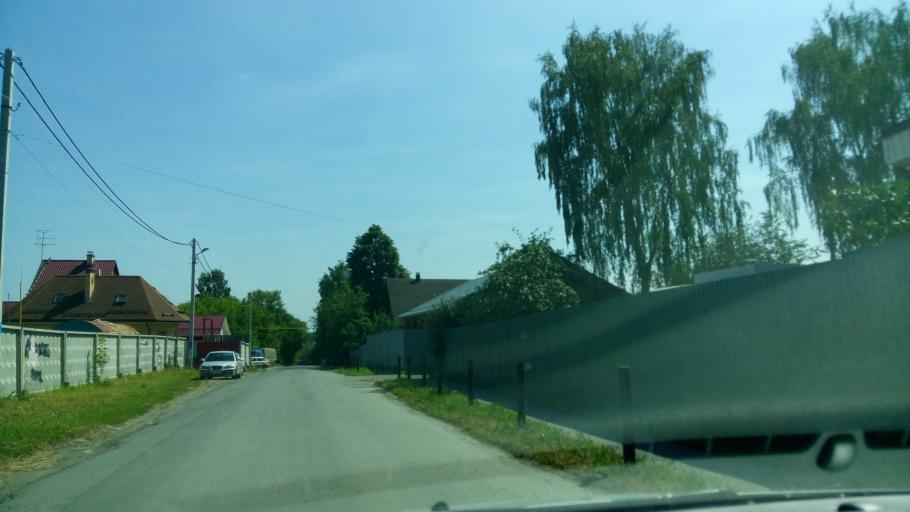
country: RU
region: Sverdlovsk
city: Yekaterinburg
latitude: 56.8761
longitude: 60.6882
